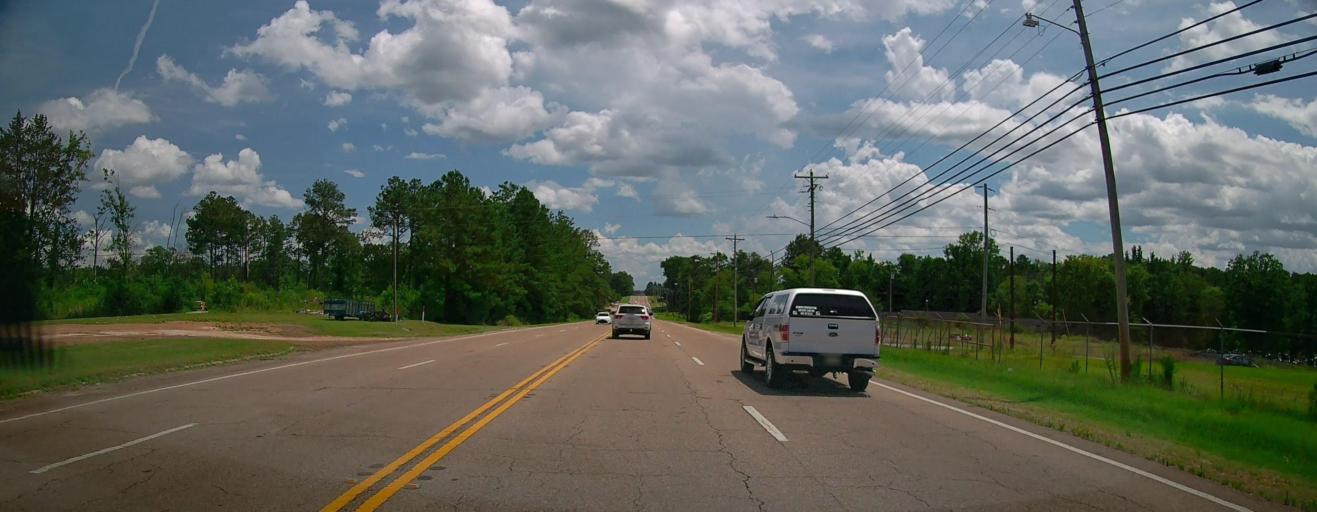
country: US
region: Mississippi
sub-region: Lee County
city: Verona
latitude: 34.1816
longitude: -88.7199
